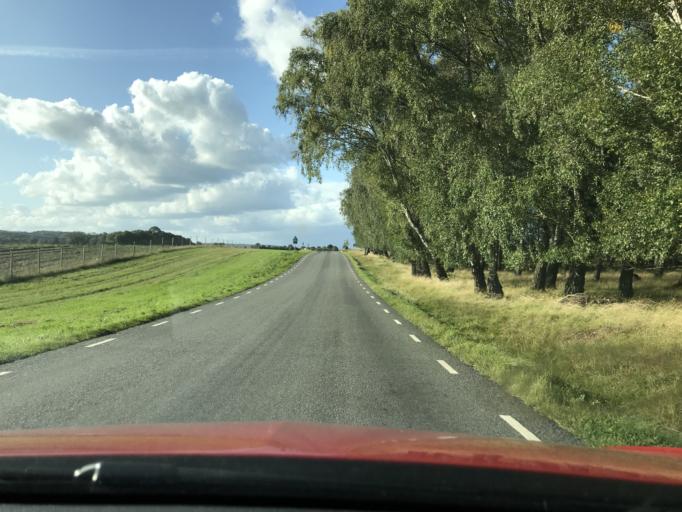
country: SE
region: Skane
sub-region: Kristianstads Kommun
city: Degeberga
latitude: 55.8605
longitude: 14.0643
